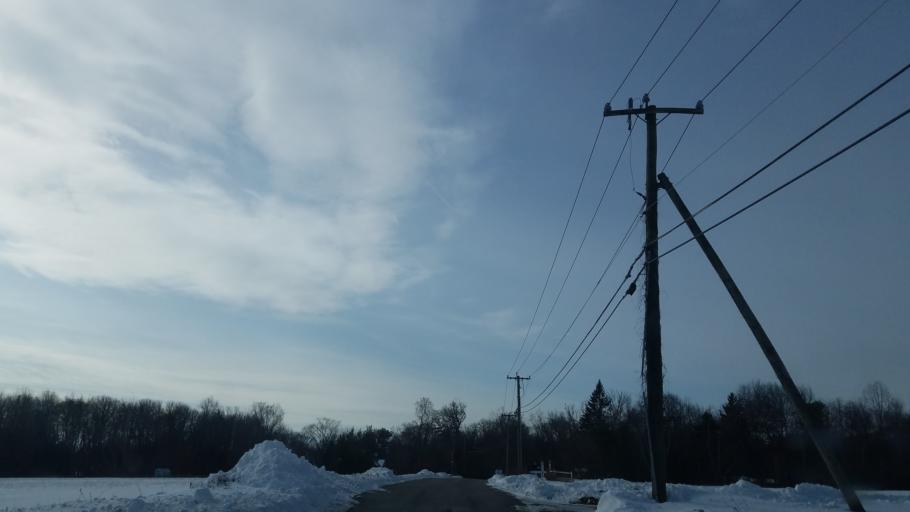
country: US
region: Connecticut
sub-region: Hartford County
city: Canton Valley
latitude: 41.8472
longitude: -72.9054
